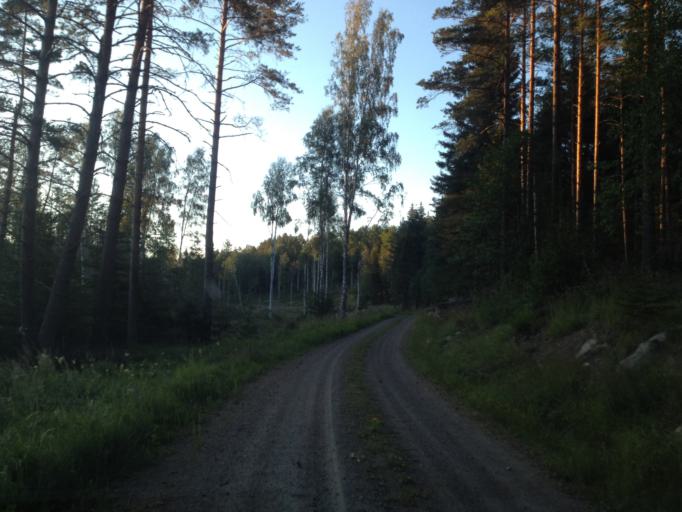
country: SE
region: Kalmar
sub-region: Vasterviks Kommun
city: Overum
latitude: 58.0063
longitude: 16.1220
